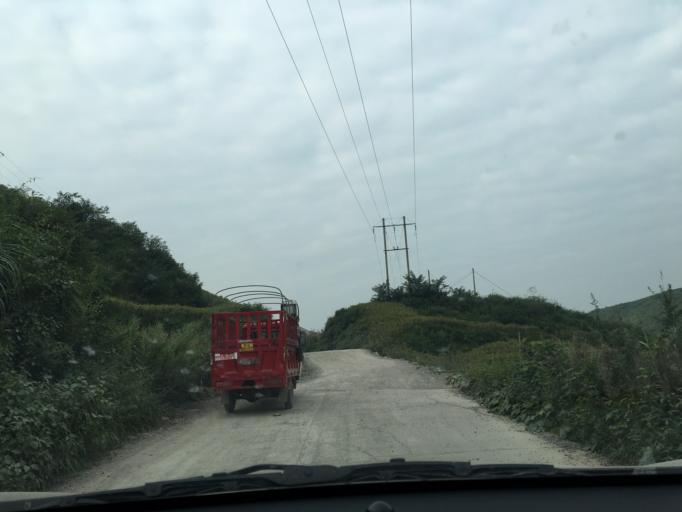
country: CN
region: Guangxi Zhuangzu Zizhiqu
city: Xinzhou
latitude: 25.4409
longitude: 105.4803
